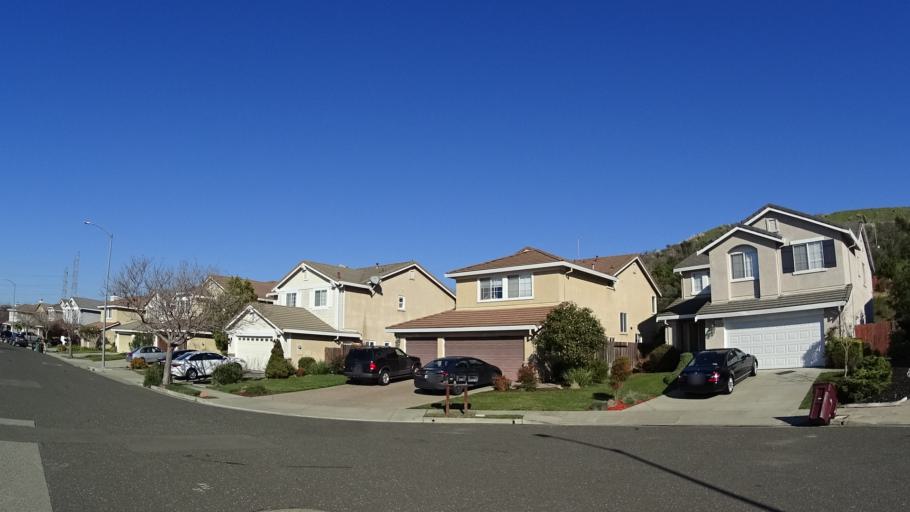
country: US
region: California
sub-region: Alameda County
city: Fairview
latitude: 37.6787
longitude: -122.0326
